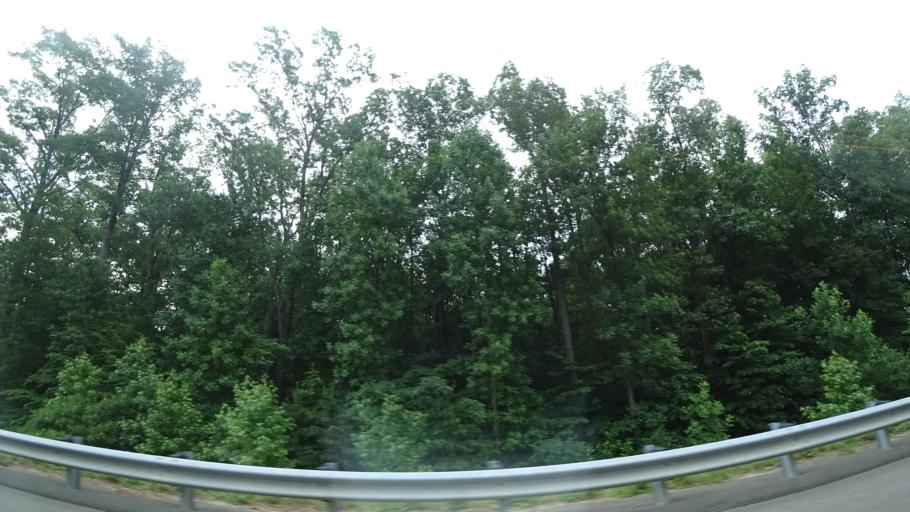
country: US
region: Virginia
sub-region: Spotsylvania County
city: Spotsylvania
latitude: 38.1948
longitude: -77.6156
